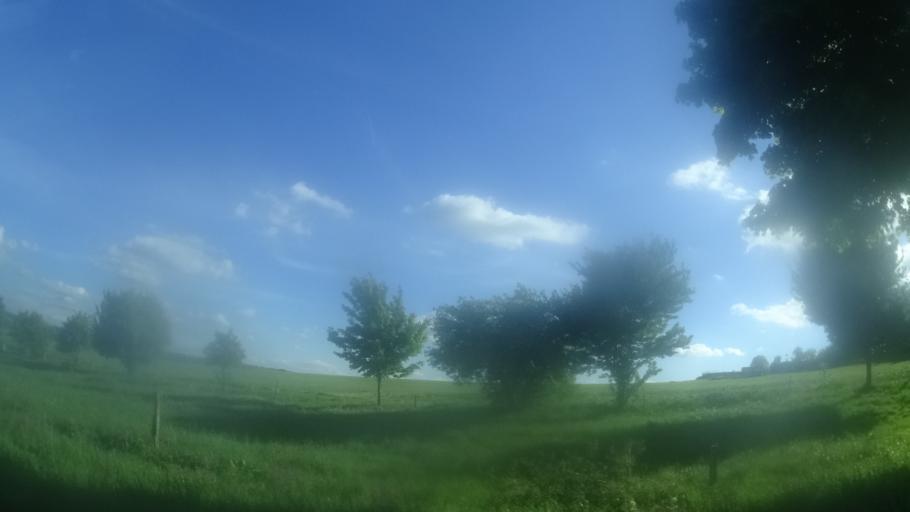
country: DE
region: Thuringia
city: Herschdorf
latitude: 50.6240
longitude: 11.0563
